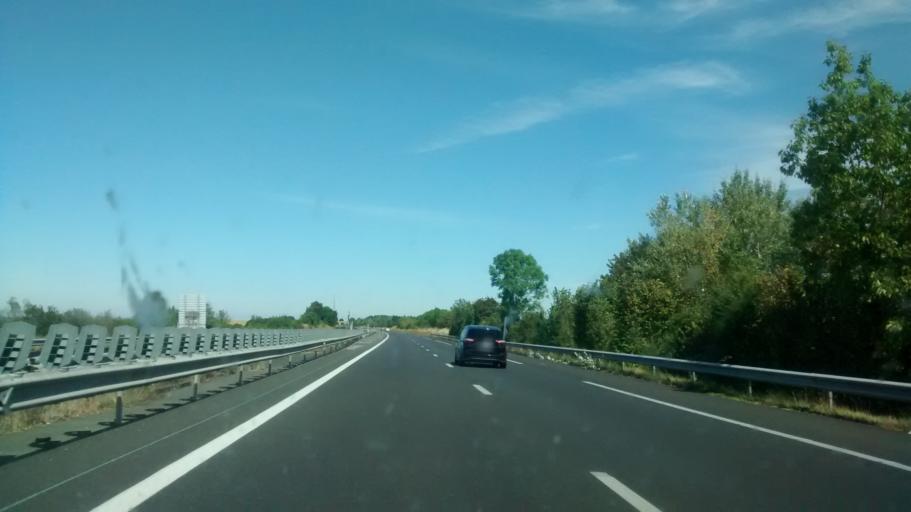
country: FR
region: Poitou-Charentes
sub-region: Departement de la Charente-Maritime
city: Saint-Jean-d'Angely
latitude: 46.0286
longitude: -0.5391
